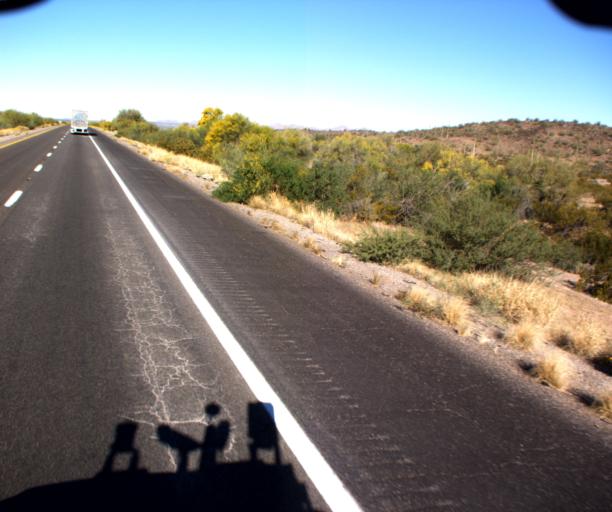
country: US
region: Arizona
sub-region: Pinal County
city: Maricopa
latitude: 32.8357
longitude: -112.1874
